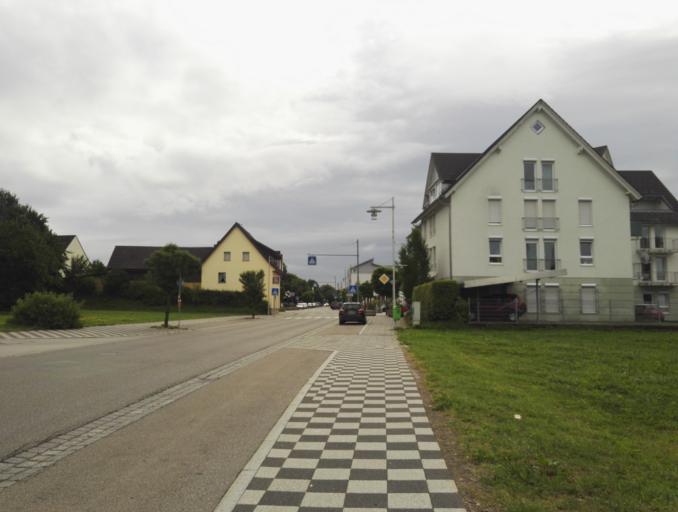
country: DE
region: Baden-Wuerttemberg
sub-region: Freiburg Region
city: Blumberg
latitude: 47.8398
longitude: 8.5335
